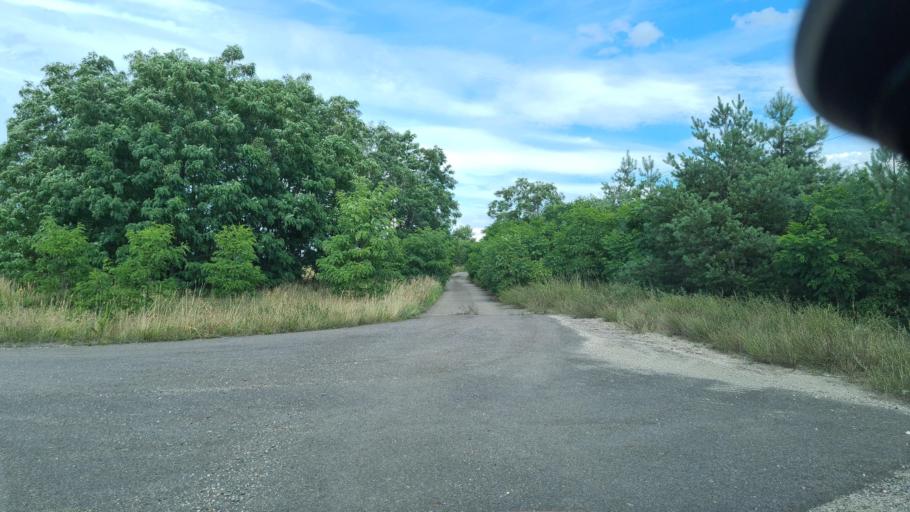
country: DE
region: Brandenburg
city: Spremberg
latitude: 51.5948
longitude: 14.3115
